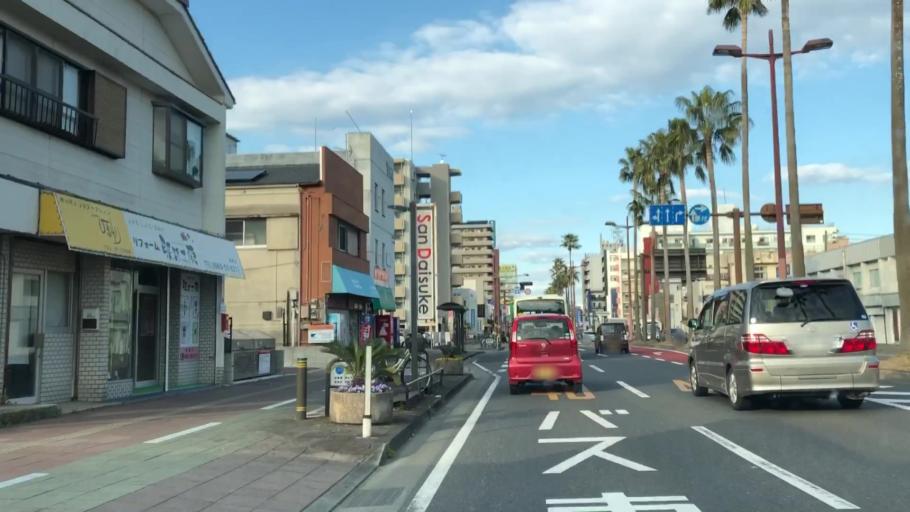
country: JP
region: Miyazaki
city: Miyazaki-shi
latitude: 31.9004
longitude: 131.4185
